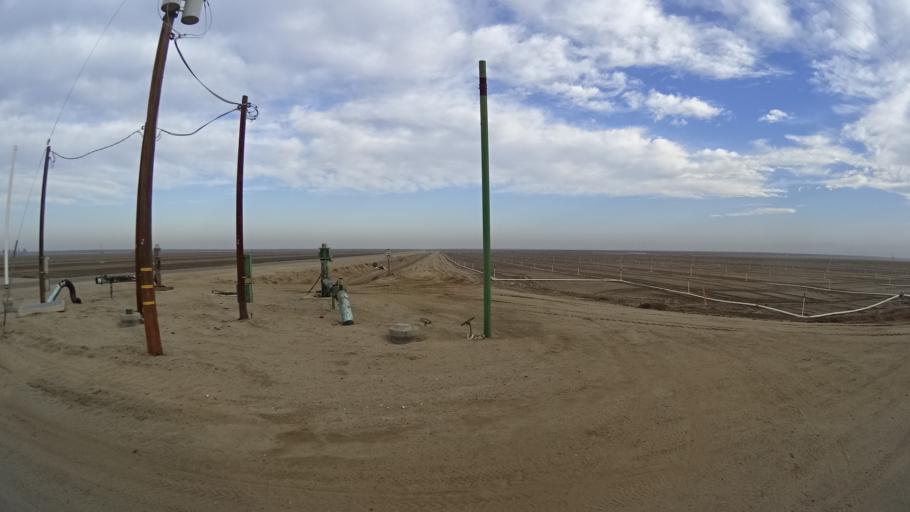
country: US
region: California
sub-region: Kern County
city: Rosedale
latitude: 35.4125
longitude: -119.1894
